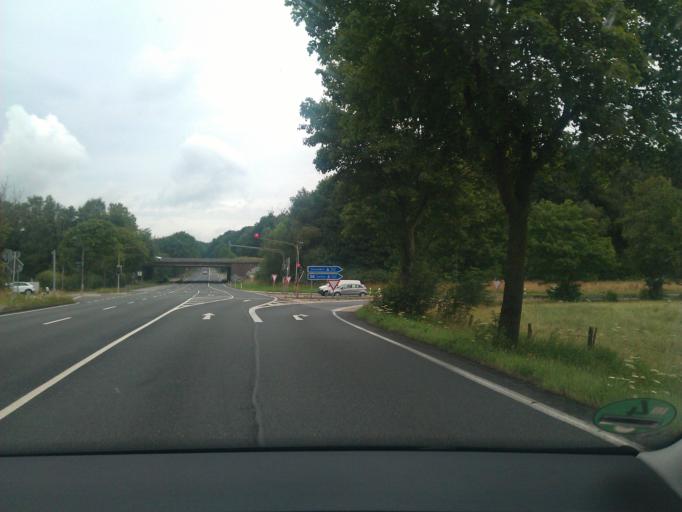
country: BE
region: Wallonia
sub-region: Province de Liege
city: Raeren
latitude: 50.7196
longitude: 6.1281
